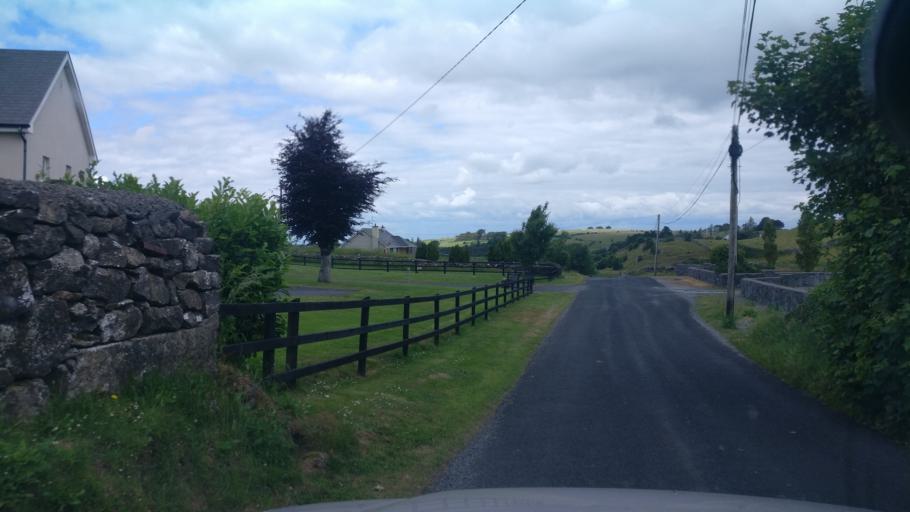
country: IE
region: Connaught
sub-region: County Galway
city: Loughrea
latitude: 53.1744
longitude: -8.5557
